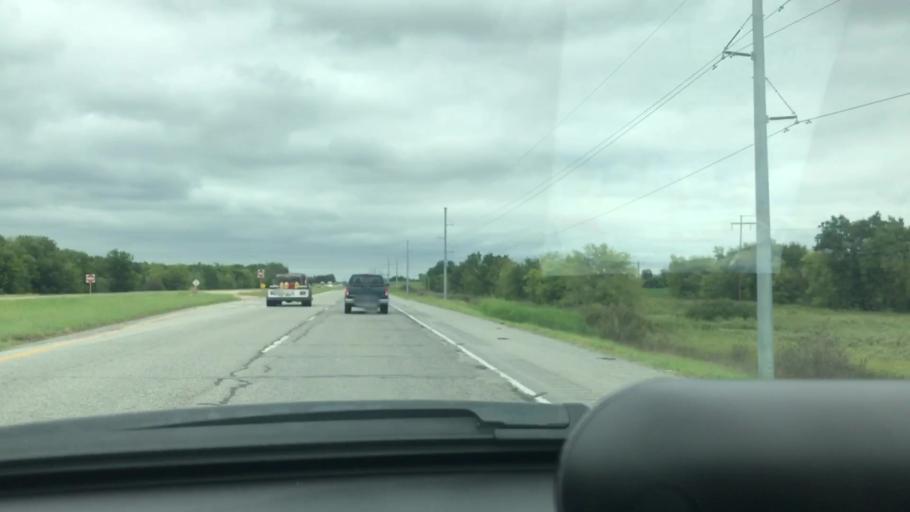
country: US
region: Oklahoma
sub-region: Wagoner County
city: Wagoner
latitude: 36.0019
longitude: -95.3685
